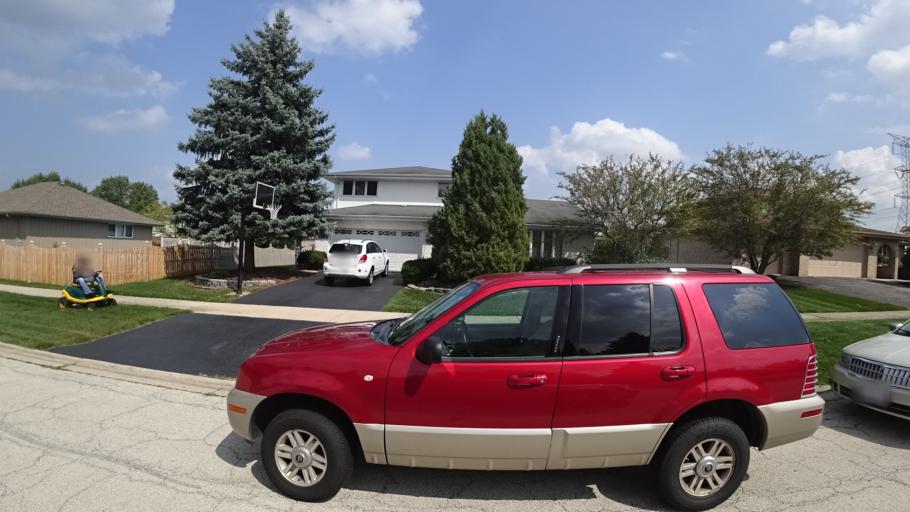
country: US
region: Illinois
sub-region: Will County
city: Goodings Grove
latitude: 41.6419
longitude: -87.9066
